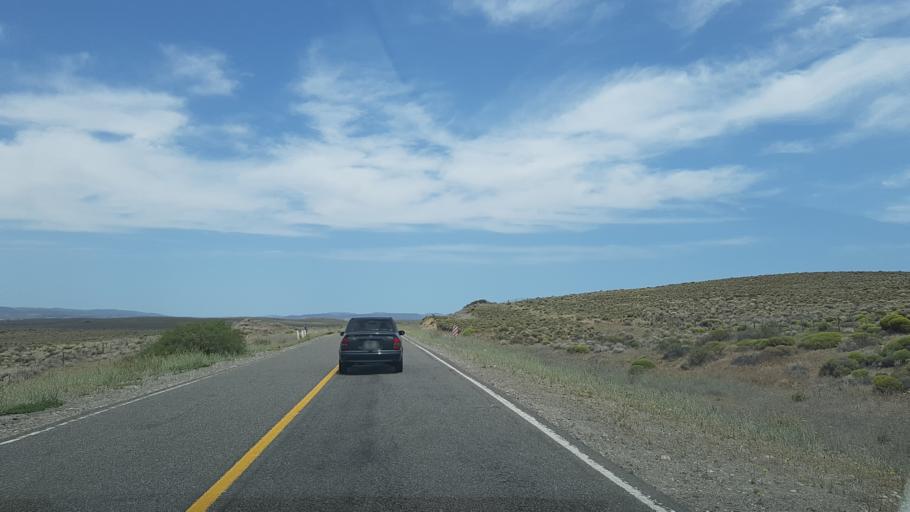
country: AR
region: Rio Negro
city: Pilcaniyeu
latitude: -40.5083
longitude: -70.6855
